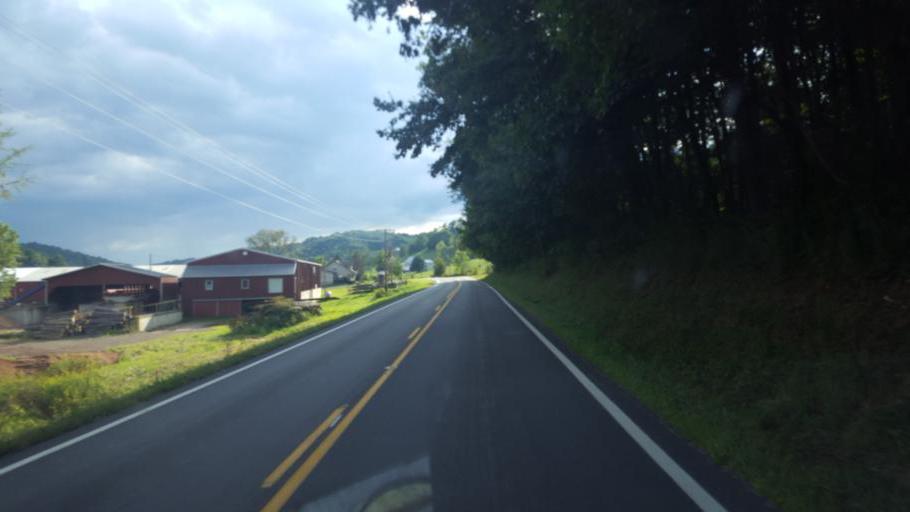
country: US
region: Ohio
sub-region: Knox County
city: Oak Hill
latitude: 40.4646
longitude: -82.0812
